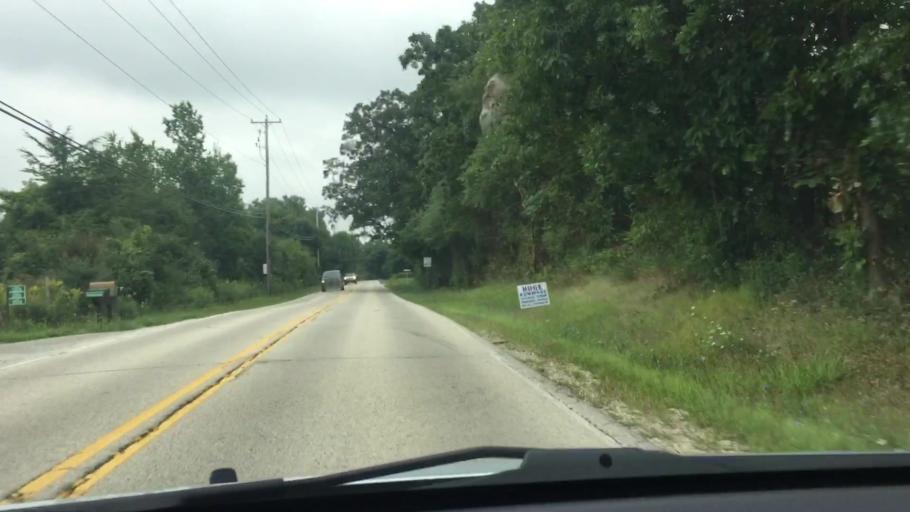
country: US
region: Wisconsin
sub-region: Waukesha County
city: Dousman
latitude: 43.0302
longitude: -88.4427
